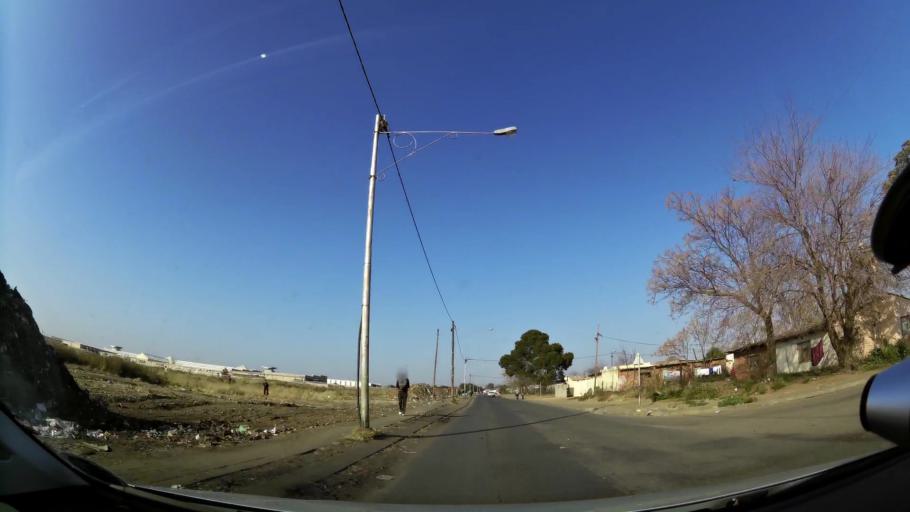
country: ZA
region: Orange Free State
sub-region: Mangaung Metropolitan Municipality
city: Bloemfontein
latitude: -29.1383
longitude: 26.2516
